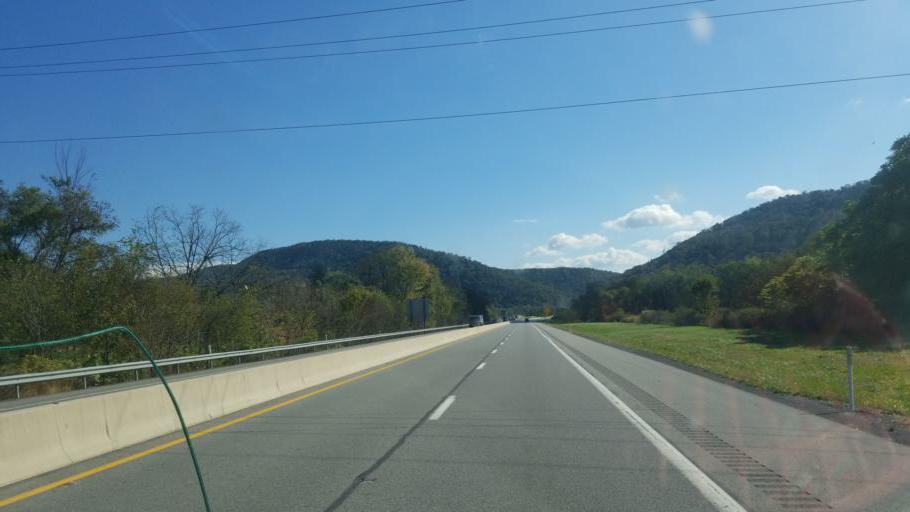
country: US
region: Pennsylvania
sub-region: Bedford County
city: Bedford
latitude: 40.0206
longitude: -78.4936
